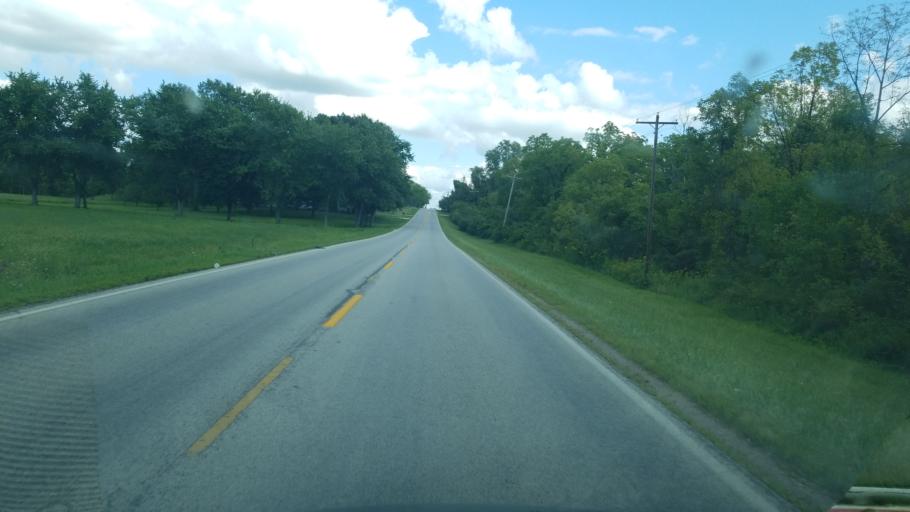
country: US
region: Ohio
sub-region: Allen County
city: Lima
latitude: 40.7885
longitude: -84.0852
